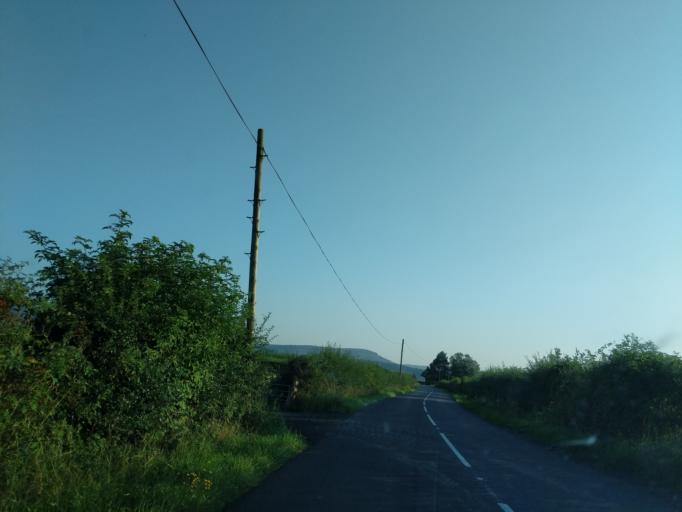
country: GB
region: Scotland
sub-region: Stirling
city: Callander
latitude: 56.1674
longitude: -4.1544
